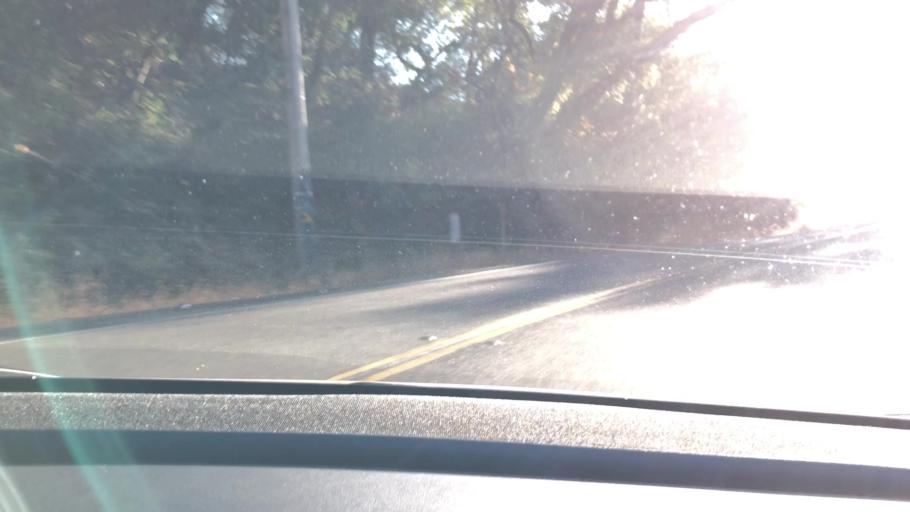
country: US
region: California
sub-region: Santa Clara County
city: Saratoga
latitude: 37.2790
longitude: -122.0712
